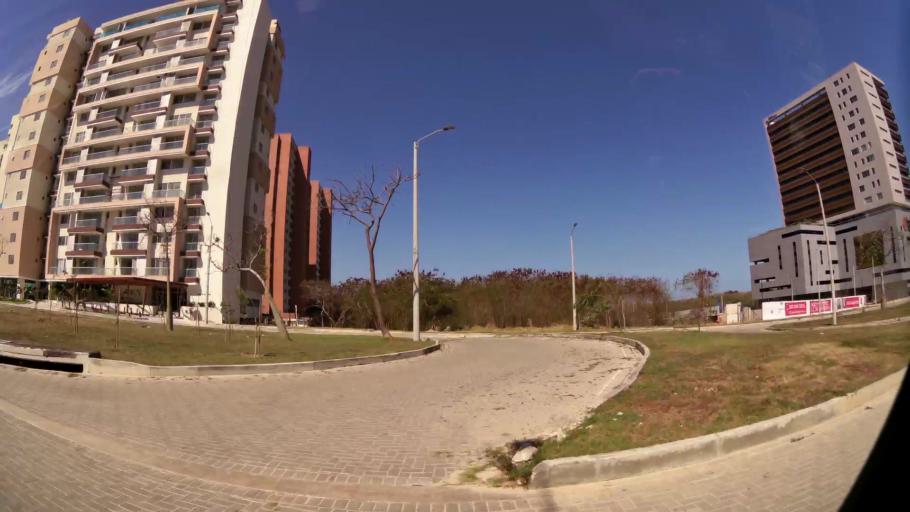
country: CO
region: Atlantico
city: Barranquilla
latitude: 11.0185
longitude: -74.8392
